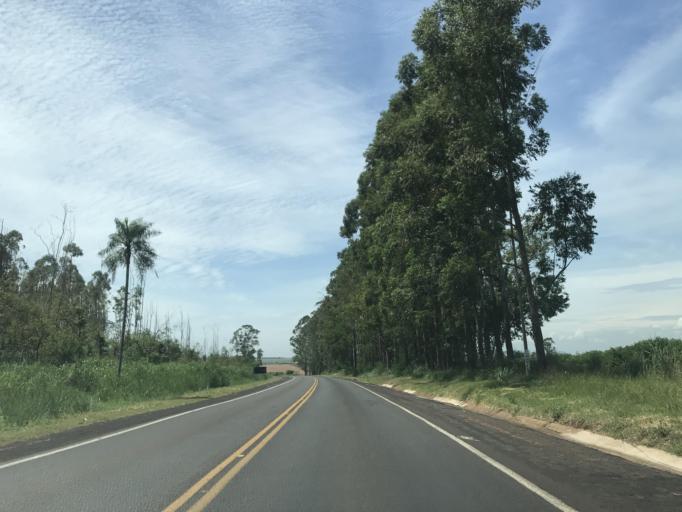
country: BR
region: Parana
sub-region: Paranavai
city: Nova Aurora
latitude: -22.9869
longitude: -52.5998
